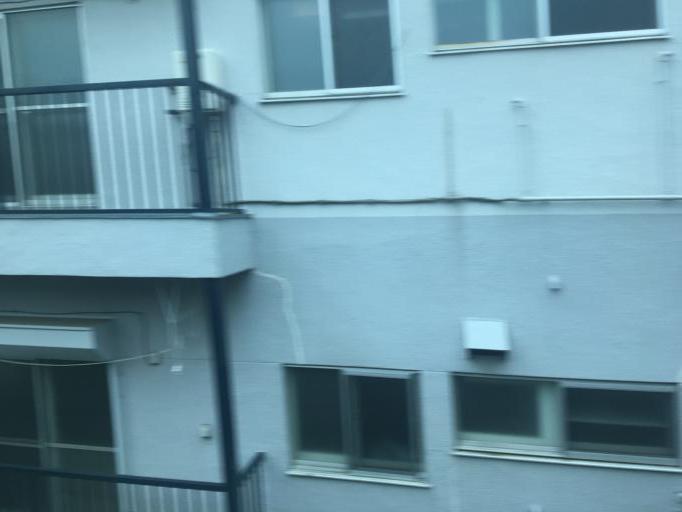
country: JP
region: Tokyo
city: Hino
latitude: 35.6979
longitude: 139.4203
